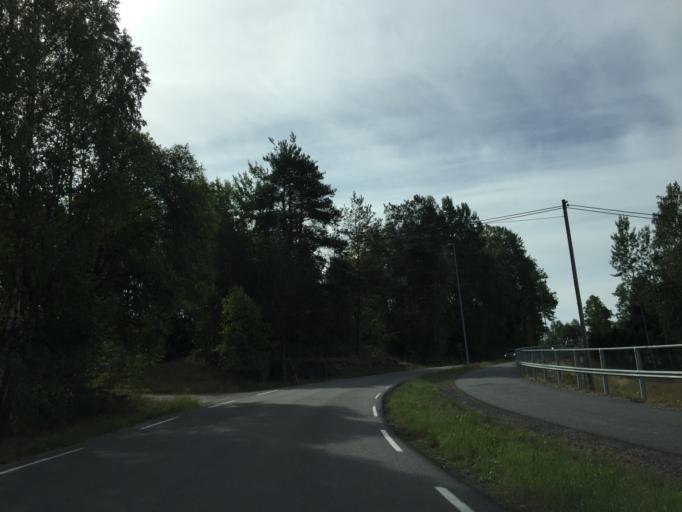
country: NO
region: Ostfold
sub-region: Moss
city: Moss
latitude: 59.4914
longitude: 10.6916
